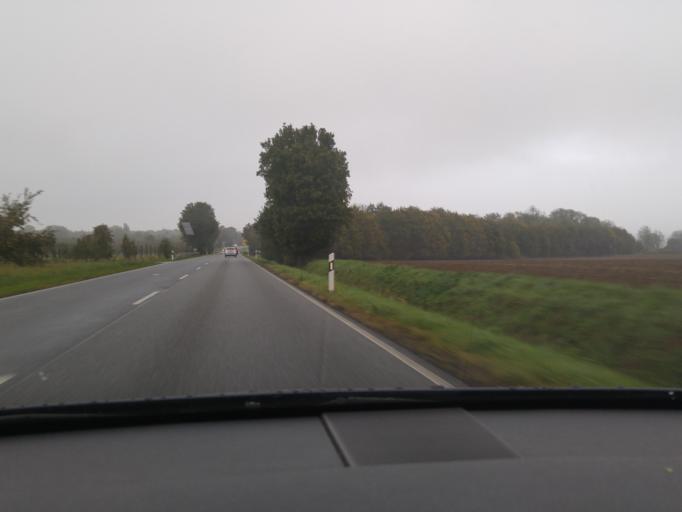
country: DE
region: Hesse
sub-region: Regierungsbezirk Darmstadt
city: Rosbach vor der Hohe
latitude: 50.3171
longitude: 8.7106
